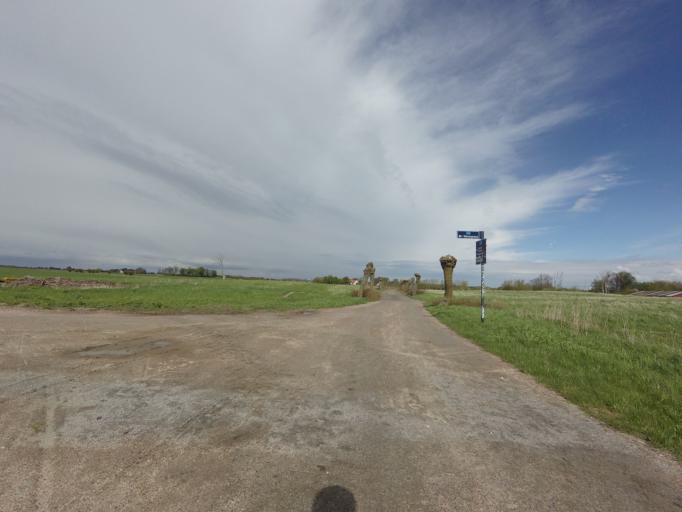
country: SE
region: Skane
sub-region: Malmo
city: Bunkeflostrand
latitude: 55.5416
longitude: 12.9707
